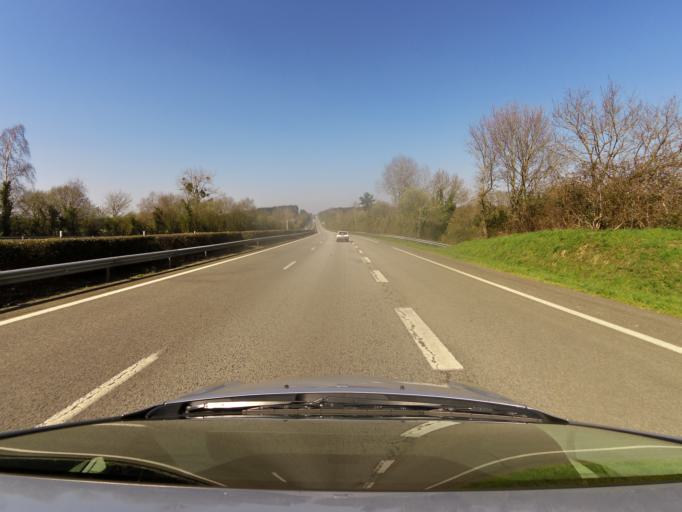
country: FR
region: Brittany
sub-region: Departement du Morbihan
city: Ploermel
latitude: 47.9333
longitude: -2.4231
